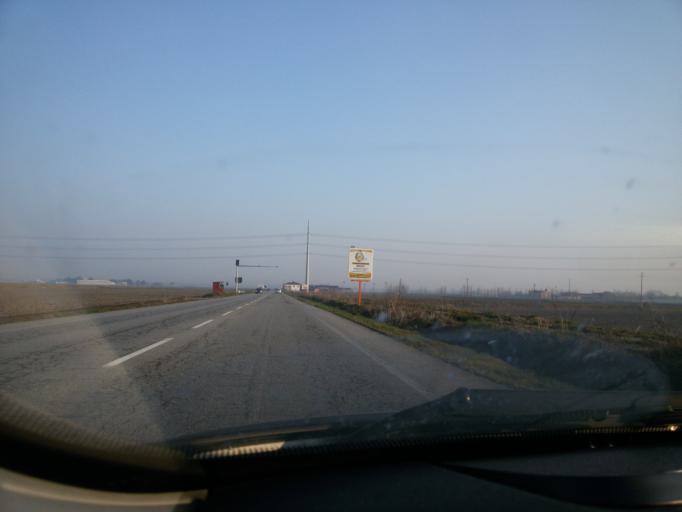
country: IT
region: Piedmont
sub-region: Provincia di Vercelli
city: Prarolo
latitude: 45.2721
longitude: 8.4637
